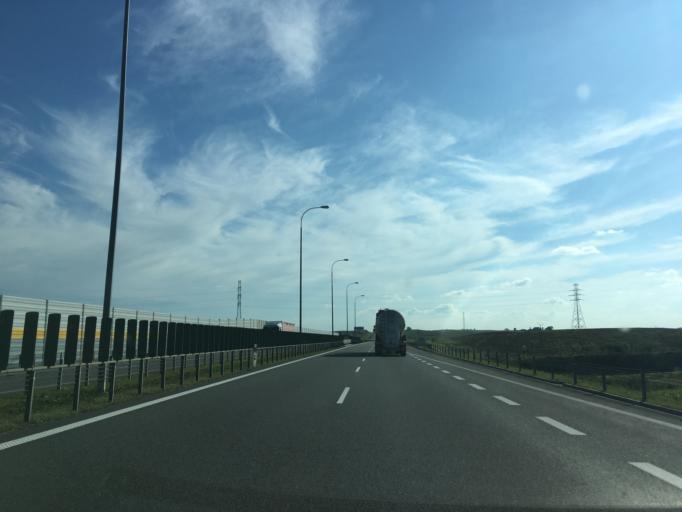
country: PL
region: Kujawsko-Pomorskie
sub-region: Powiat chelminski
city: Lisewo
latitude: 53.3363
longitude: 18.7090
